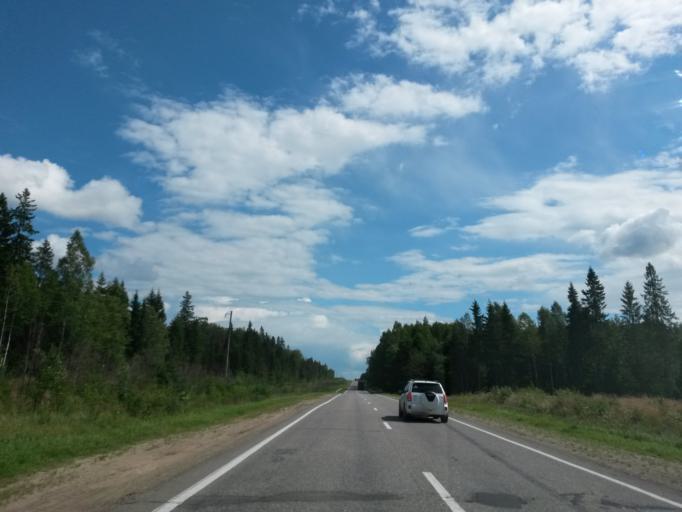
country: RU
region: Jaroslavl
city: Gavrilov-Yam
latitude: 57.2665
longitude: 39.9963
